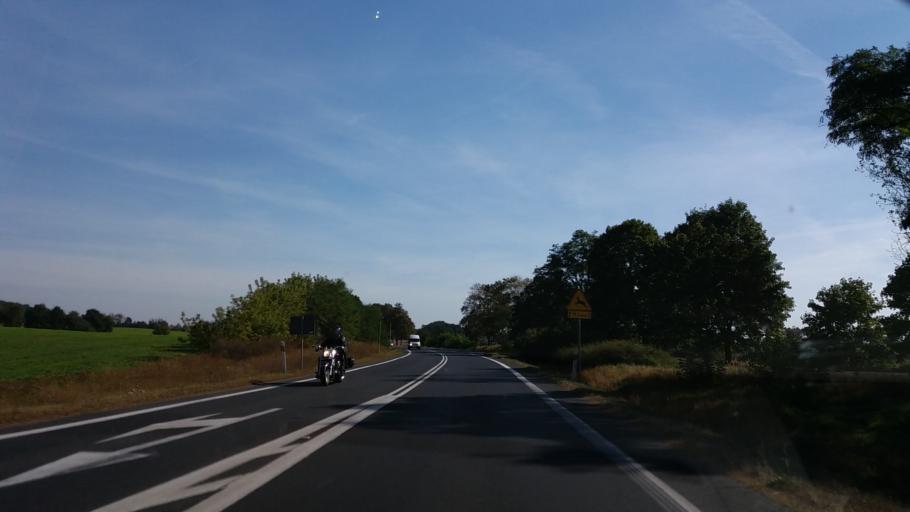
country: PL
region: Greater Poland Voivodeship
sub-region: Powiat miedzychodzki
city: Kwilcz
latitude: 52.5490
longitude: 16.1091
